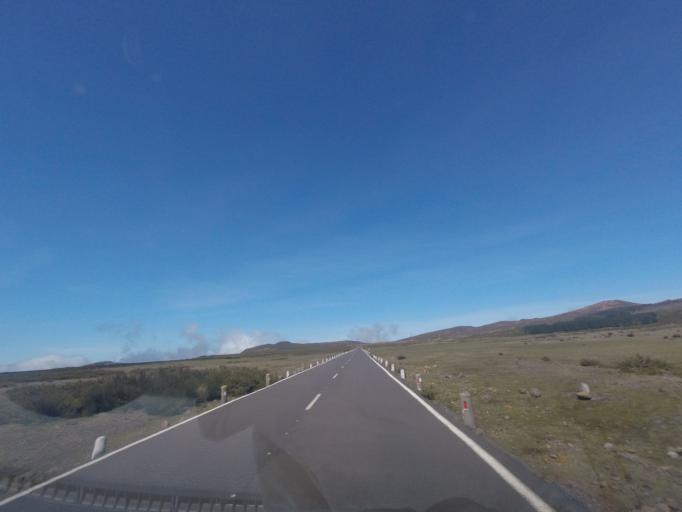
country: PT
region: Madeira
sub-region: Calheta
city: Arco da Calheta
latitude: 32.7472
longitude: -17.0980
